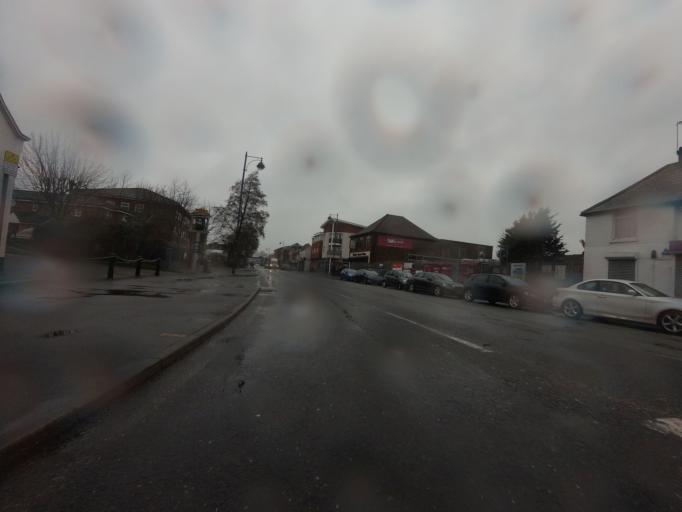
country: GB
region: England
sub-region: Hertfordshire
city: Waltham Cross
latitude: 51.6899
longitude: -0.0337
